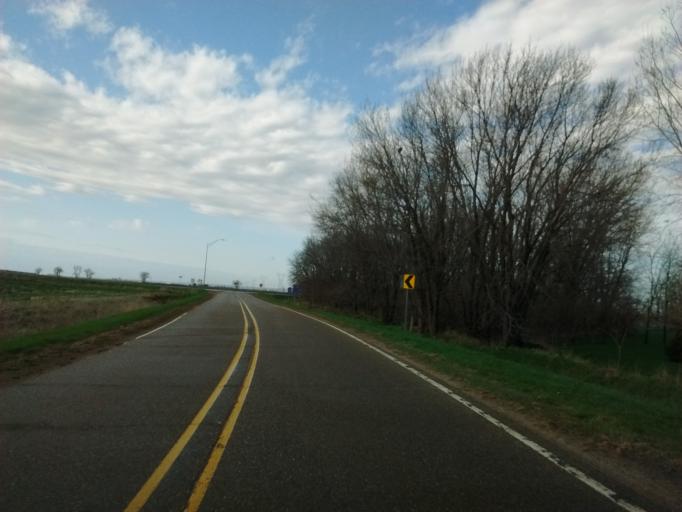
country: US
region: Iowa
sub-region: Woodbury County
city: Sergeant Bluff
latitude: 42.3996
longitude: -96.2351
